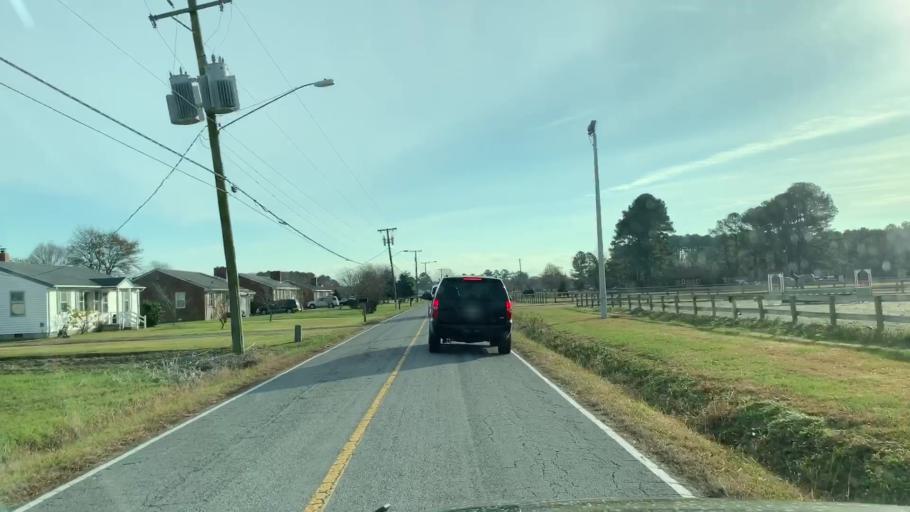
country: US
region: Virginia
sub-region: City of Virginia Beach
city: Virginia Beach
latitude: 36.6901
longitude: -76.0096
